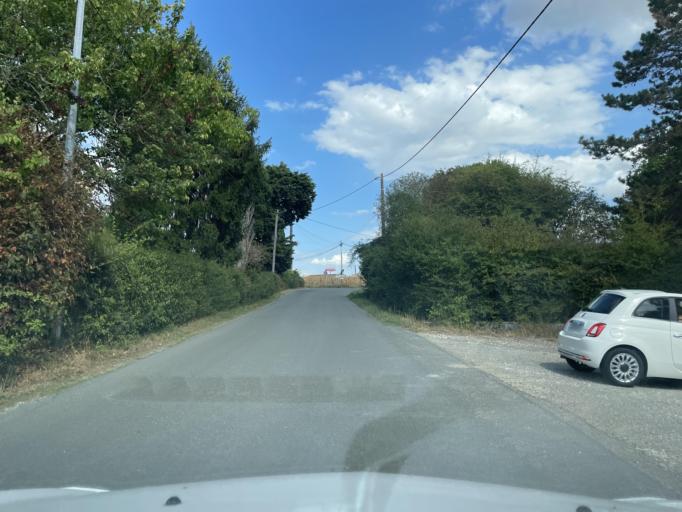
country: FR
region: Aquitaine
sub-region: Departement du Lot-et-Garonne
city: Casteljaloux
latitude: 44.3165
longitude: 0.0998
